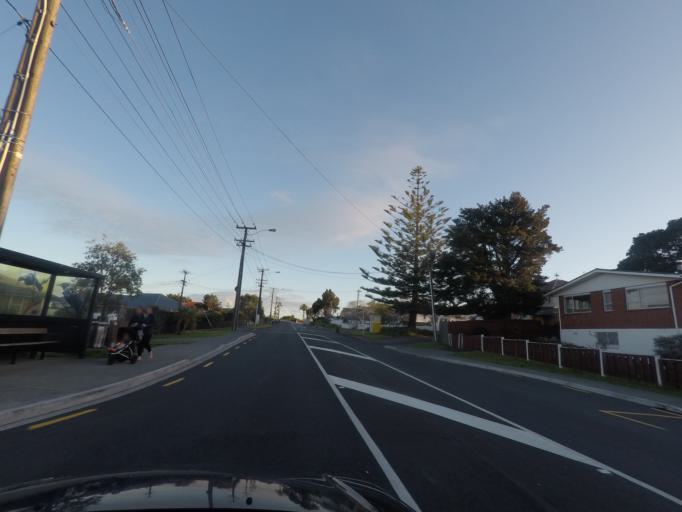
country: NZ
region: Auckland
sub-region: Auckland
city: Rosebank
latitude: -36.8829
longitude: 174.6458
